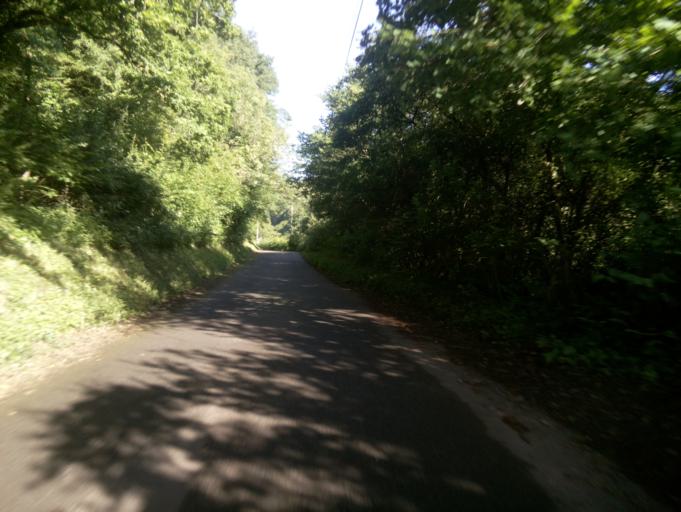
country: GB
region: Wales
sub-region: Monmouthshire
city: Tintern
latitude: 51.6995
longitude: -2.7060
